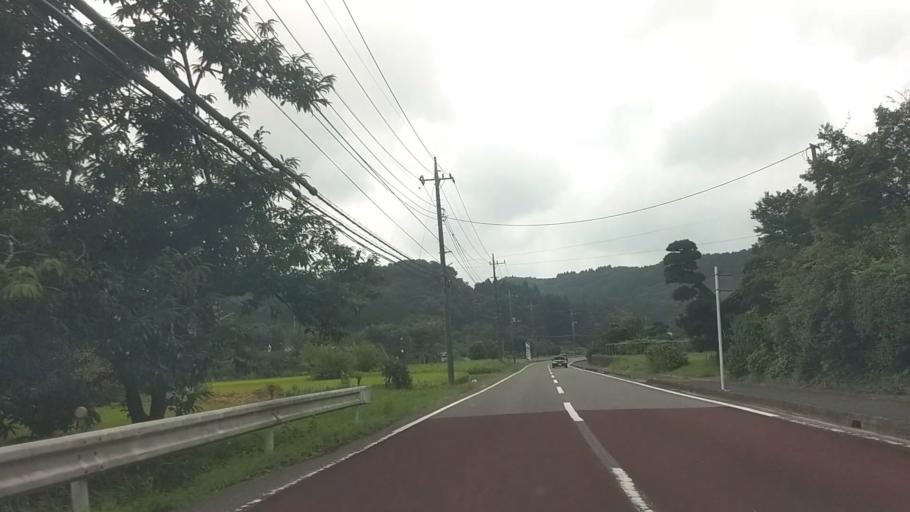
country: JP
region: Chiba
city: Kawaguchi
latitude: 35.2278
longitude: 140.0807
